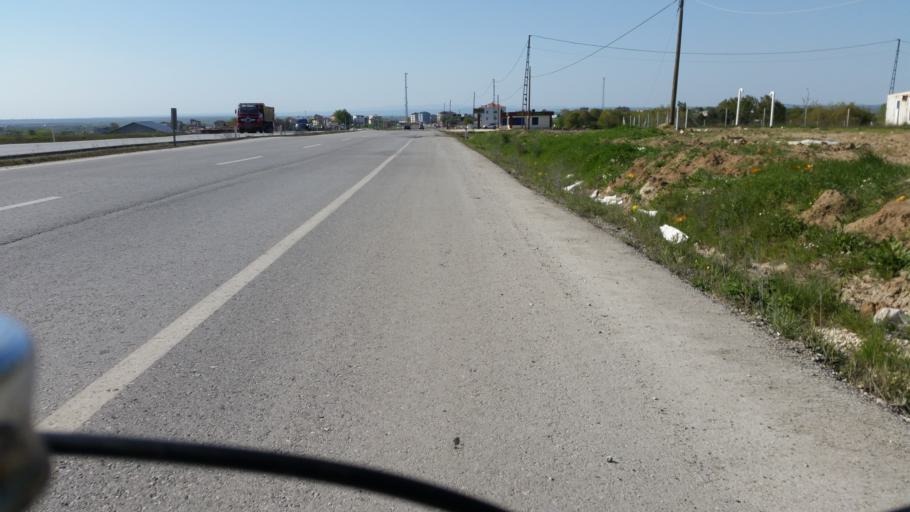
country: TR
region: Tekirdag
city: Cerkezkoey
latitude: 41.3487
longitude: 27.9592
